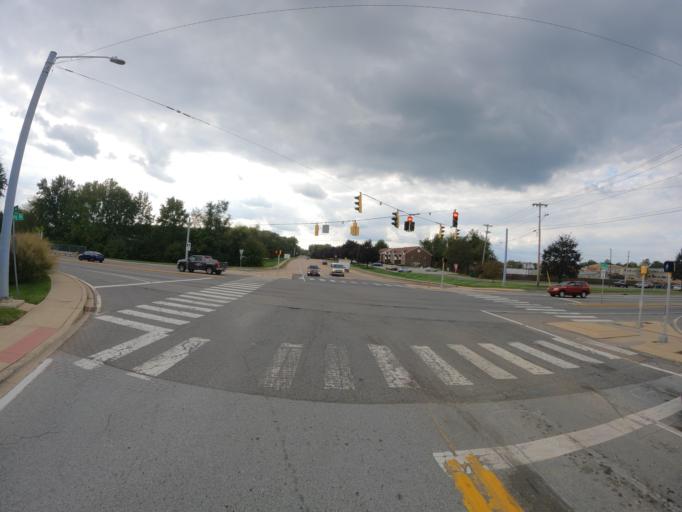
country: US
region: Delaware
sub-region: New Castle County
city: Brookside
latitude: 39.6788
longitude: -75.7354
